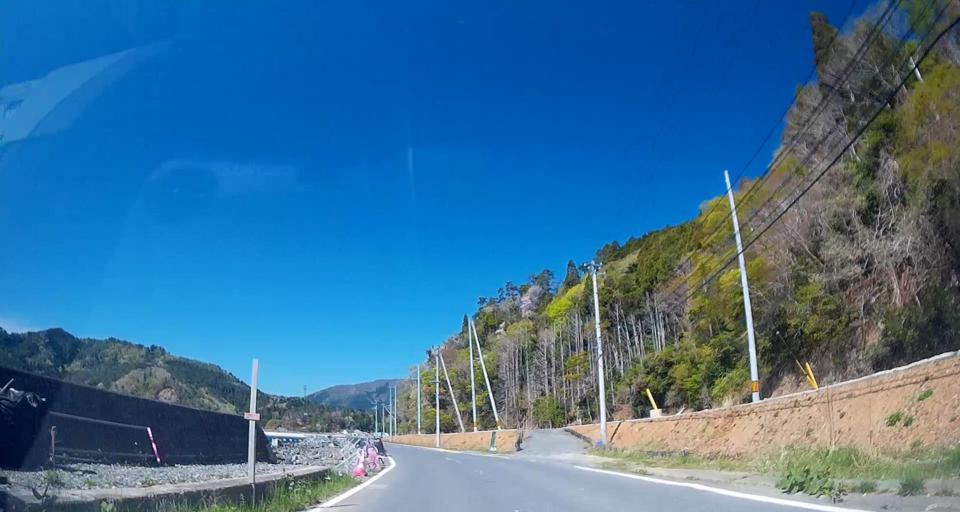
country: JP
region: Miyagi
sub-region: Oshika Gun
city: Onagawa Cho
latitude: 38.5202
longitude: 141.4816
